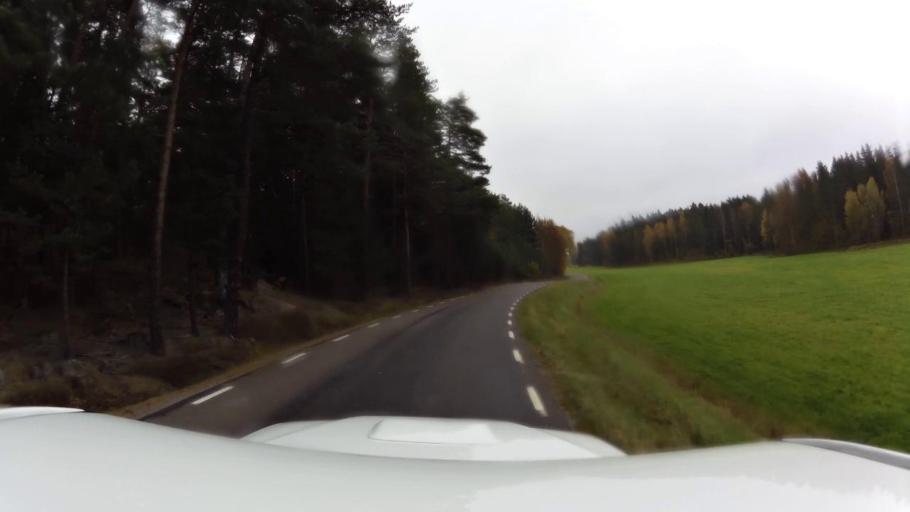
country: SE
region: OEstergoetland
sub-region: Linkopings Kommun
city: Linghem
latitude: 58.3533
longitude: 15.8566
